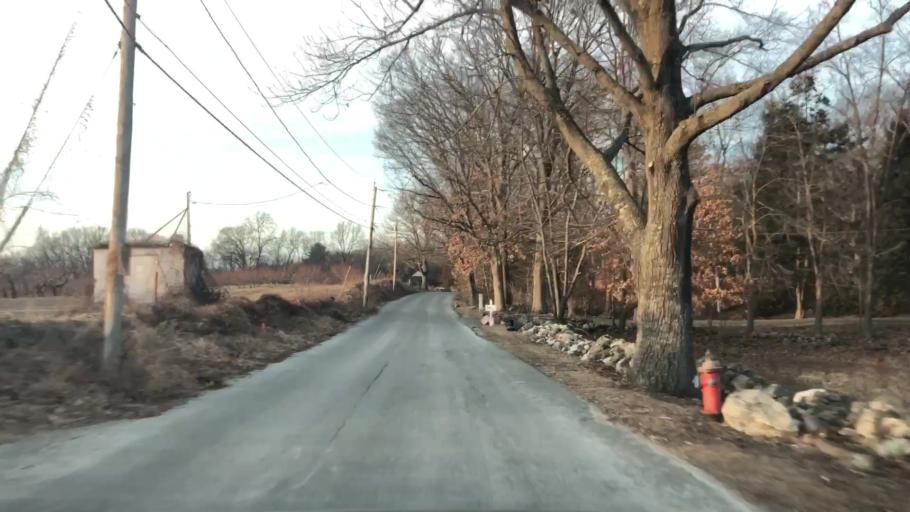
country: US
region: Massachusetts
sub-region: Essex County
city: North Andover
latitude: 42.6912
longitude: -71.0756
